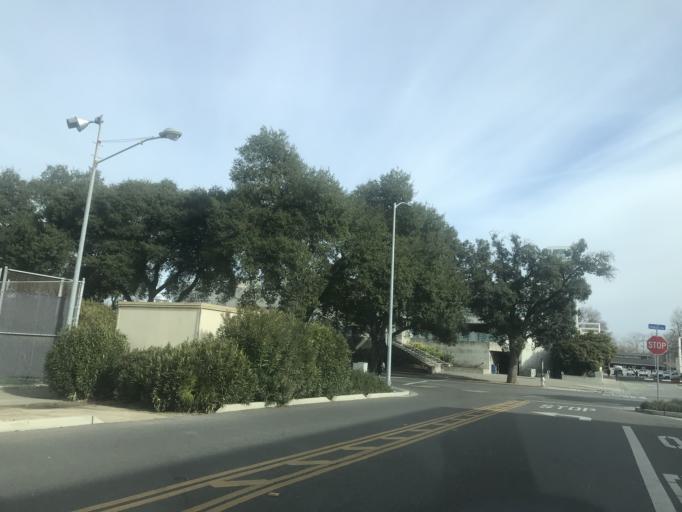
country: US
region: California
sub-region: Yolo County
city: Davis
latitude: 38.5440
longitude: -121.7507
